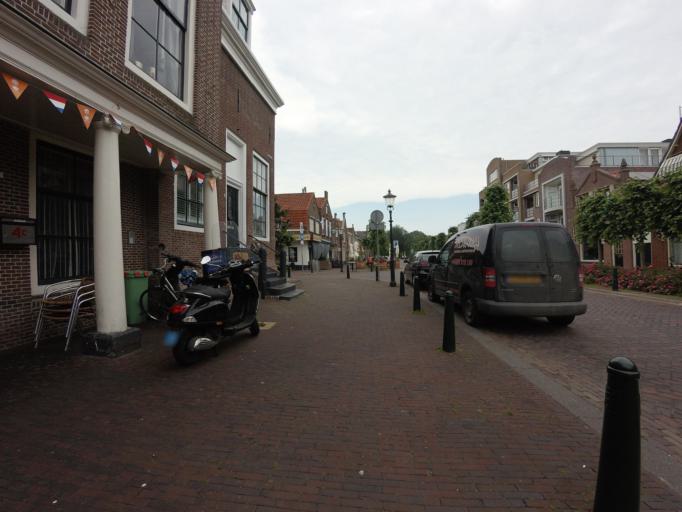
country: NL
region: North Holland
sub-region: Gemeente Enkhuizen
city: Enkhuizen
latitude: 52.7052
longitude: 5.2936
